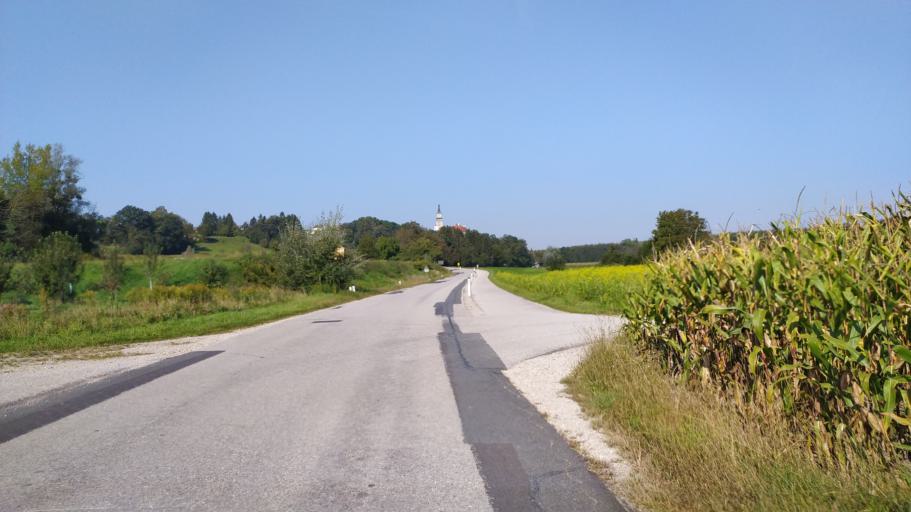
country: AT
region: Lower Austria
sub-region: Politischer Bezirk Amstetten
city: Zeillern
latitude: 48.1642
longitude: 14.7256
